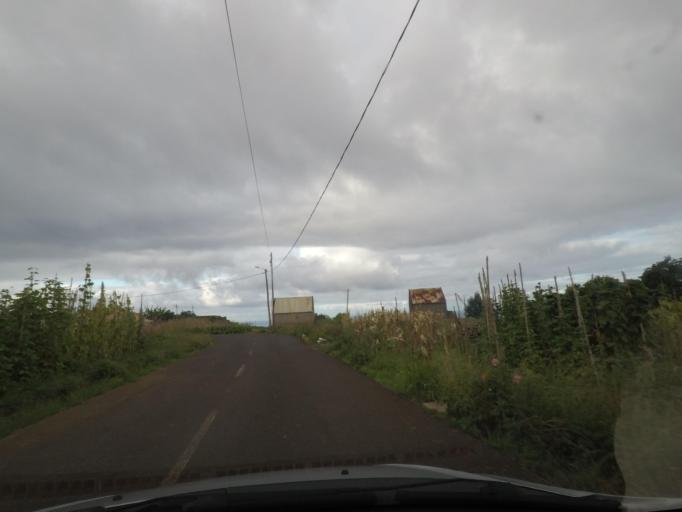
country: PT
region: Madeira
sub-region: Santana
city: Santana
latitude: 32.8152
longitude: -16.8787
